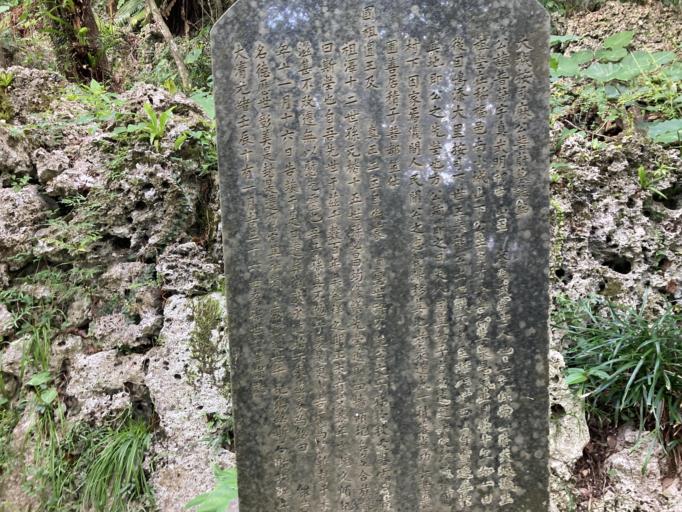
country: JP
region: Okinawa
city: Tomigusuku
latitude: 26.1679
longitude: 127.7644
